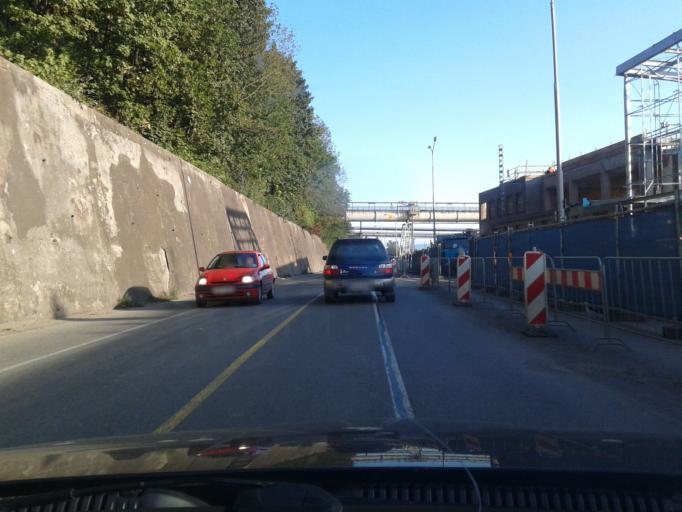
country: CZ
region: Moravskoslezsky
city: Trinec
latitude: 49.6879
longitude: 18.6622
